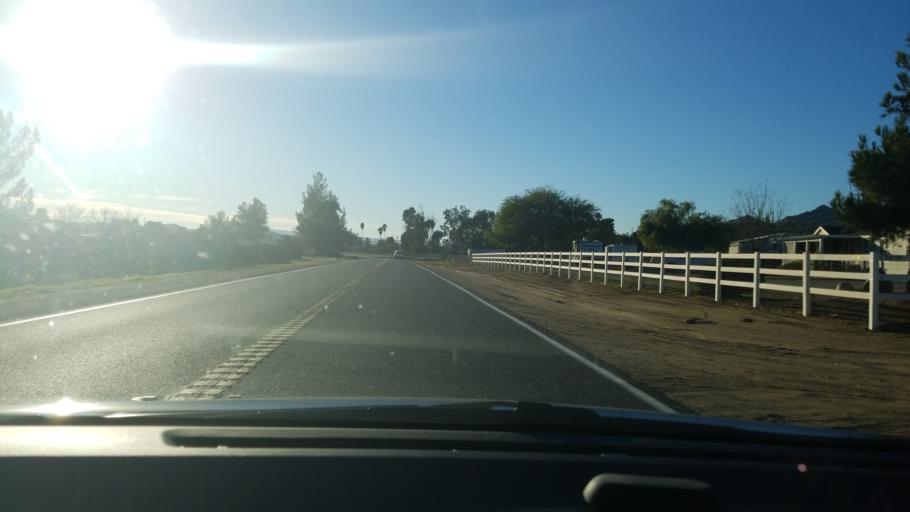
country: US
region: California
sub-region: Riverside County
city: Winchester
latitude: 33.7140
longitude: -117.0807
